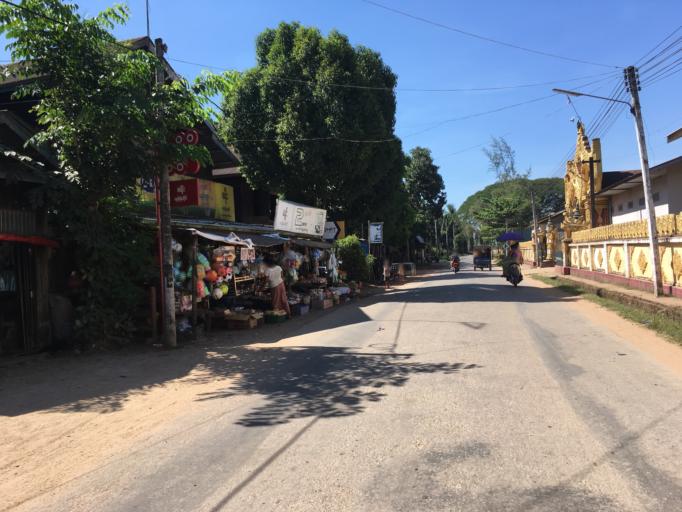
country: MM
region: Mon
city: Kyaikkami
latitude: 15.5091
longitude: 97.8548
